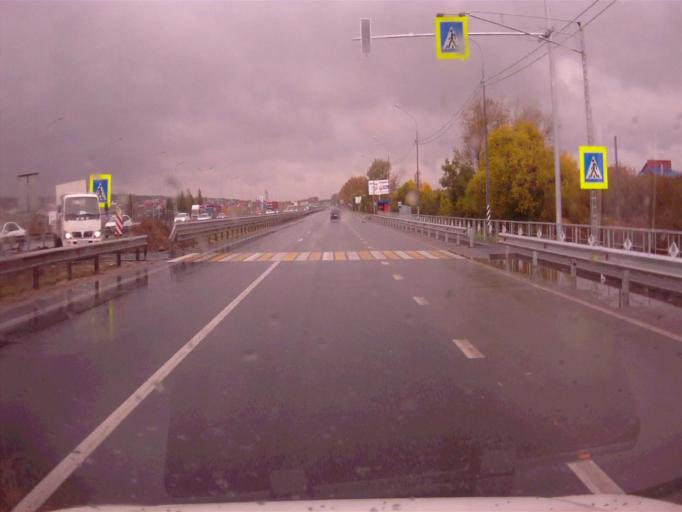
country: RU
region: Chelyabinsk
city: Dolgoderevenskoye
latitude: 55.2747
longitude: 61.3440
